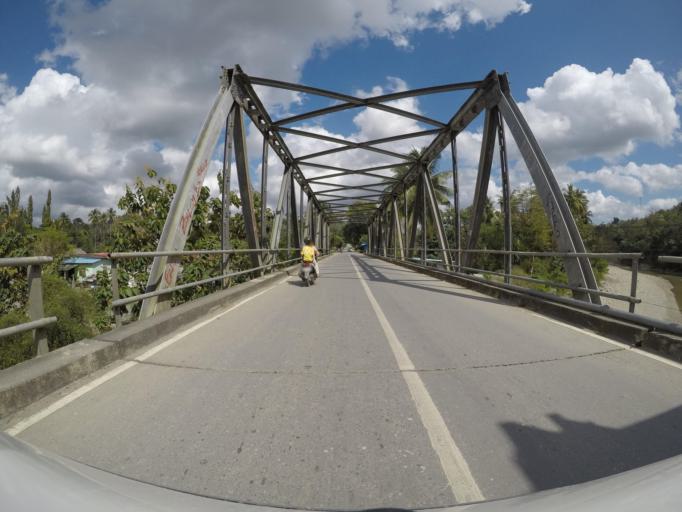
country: TL
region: Viqueque
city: Viqueque
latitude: -8.8681
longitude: 126.3697
